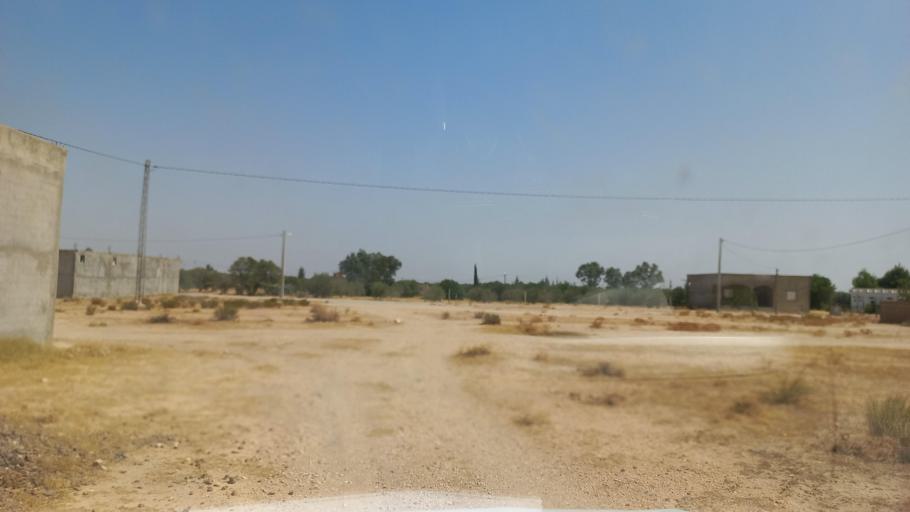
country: TN
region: Al Qasrayn
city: Kasserine
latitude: 35.2504
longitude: 9.0231
